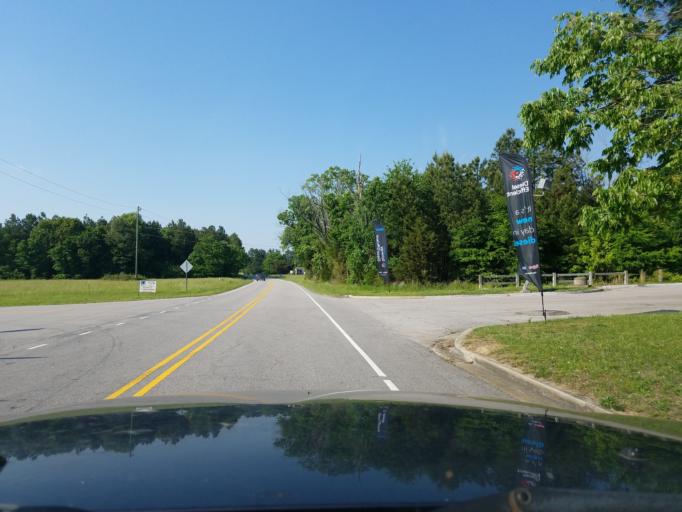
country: US
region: North Carolina
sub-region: Vance County
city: Henderson
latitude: 36.3637
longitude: -78.3739
